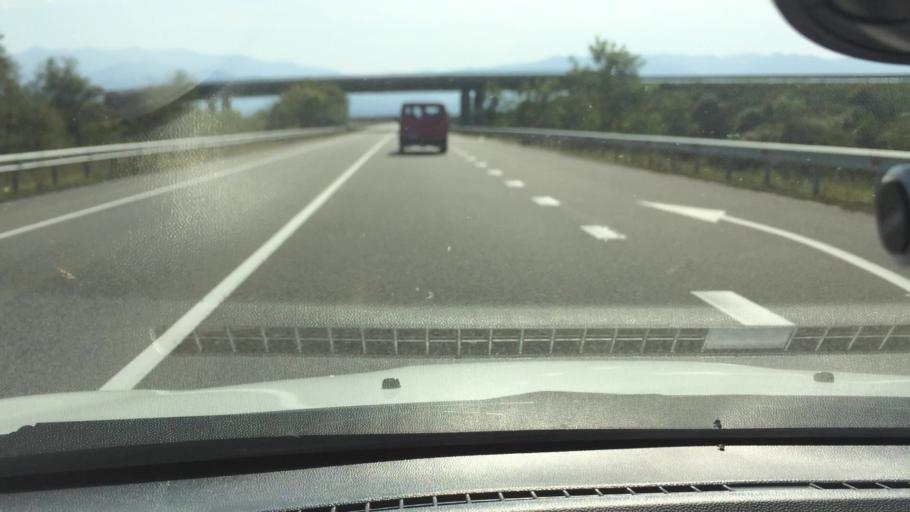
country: GE
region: Ajaria
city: Ochkhamuri
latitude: 41.8996
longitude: 41.7960
